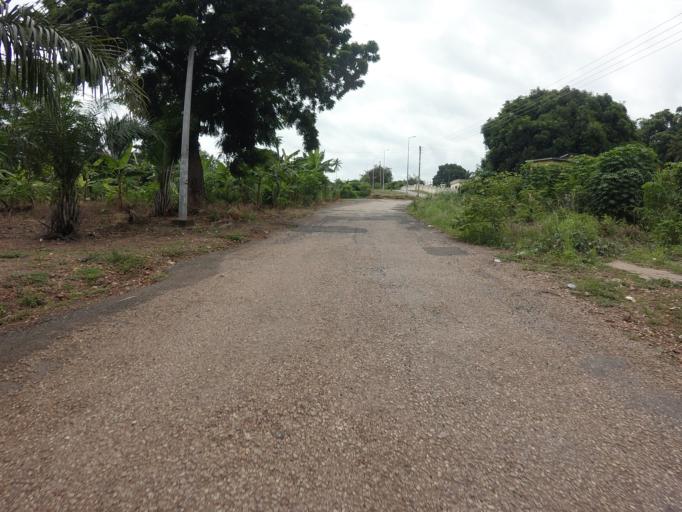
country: GH
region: Volta
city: Ho
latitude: 6.6037
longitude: 0.4621
